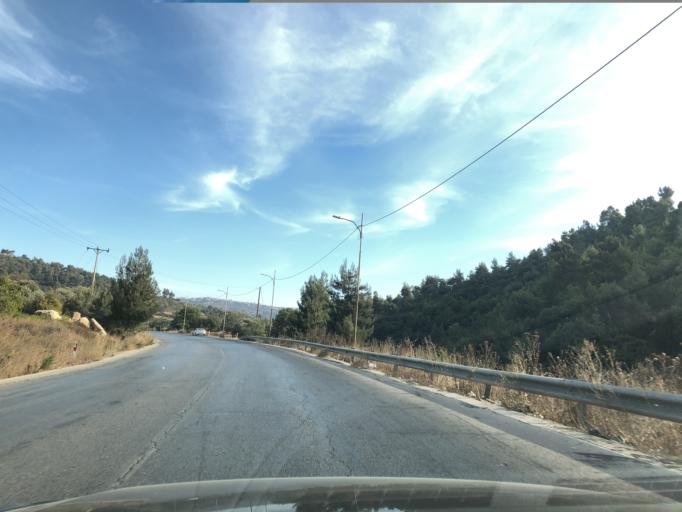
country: JO
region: Irbid
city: Sakib
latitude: 32.2882
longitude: 35.7919
